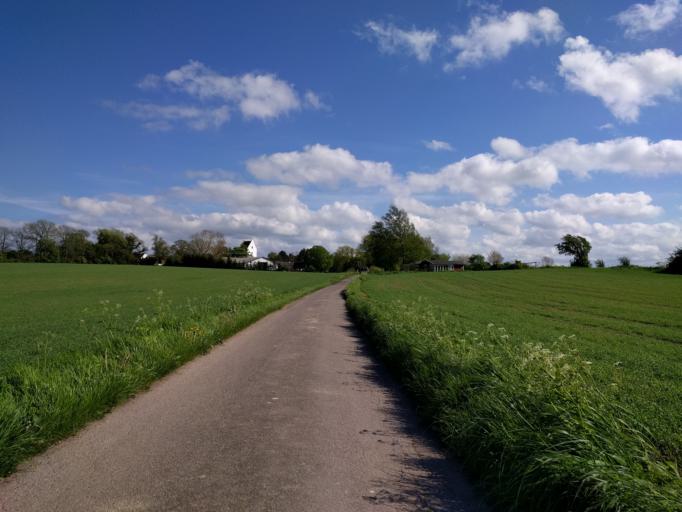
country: DK
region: Zealand
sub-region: Guldborgsund Kommune
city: Stubbekobing
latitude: 54.9344
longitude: 12.0450
